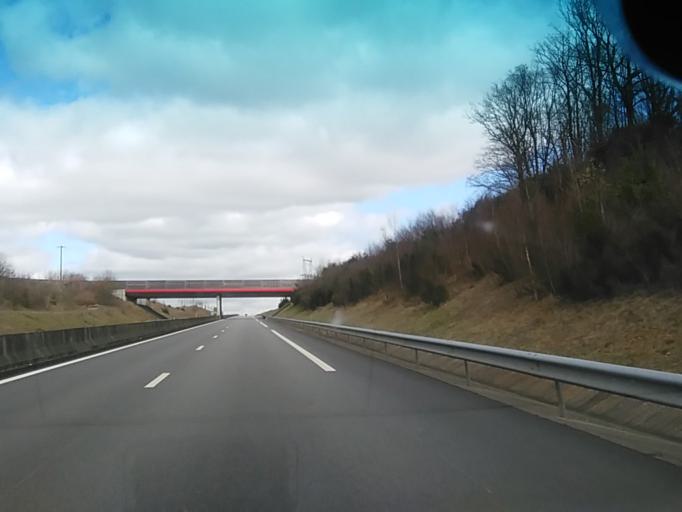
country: FR
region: Haute-Normandie
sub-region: Departement de l'Eure
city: Bourg-Achard
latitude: 49.2860
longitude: 0.7824
